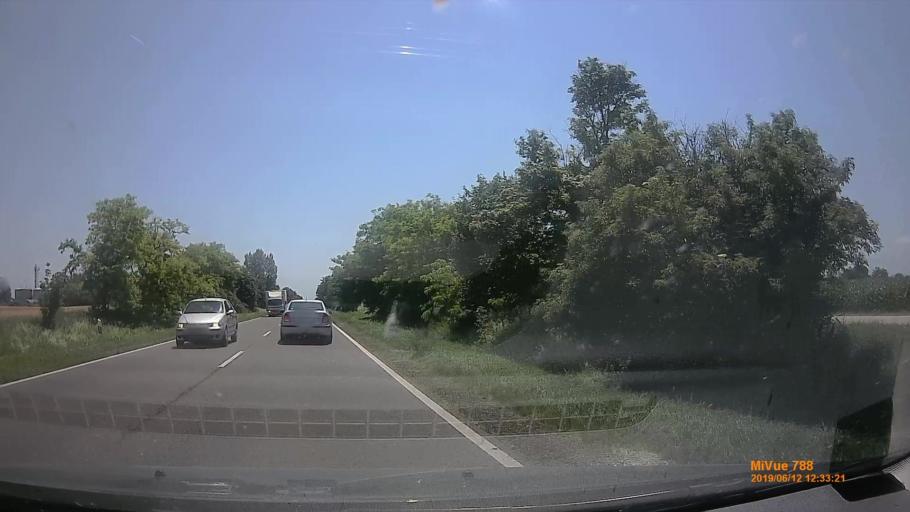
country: HU
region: Bacs-Kiskun
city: Varosfoeld
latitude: 46.8345
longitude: 19.7561
